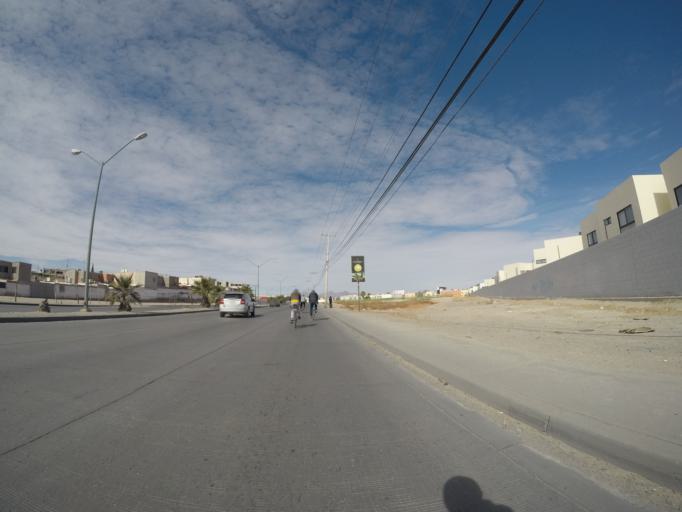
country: MX
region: Chihuahua
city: Ciudad Juarez
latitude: 31.6729
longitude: -106.4045
